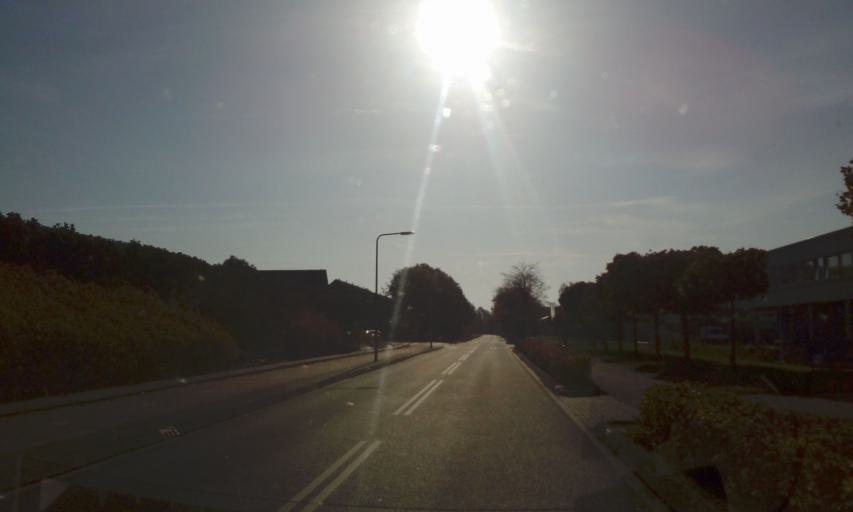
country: NL
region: South Holland
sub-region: Gemeente Lansingerland
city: Bleiswijk
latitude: 52.0143
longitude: 4.5441
